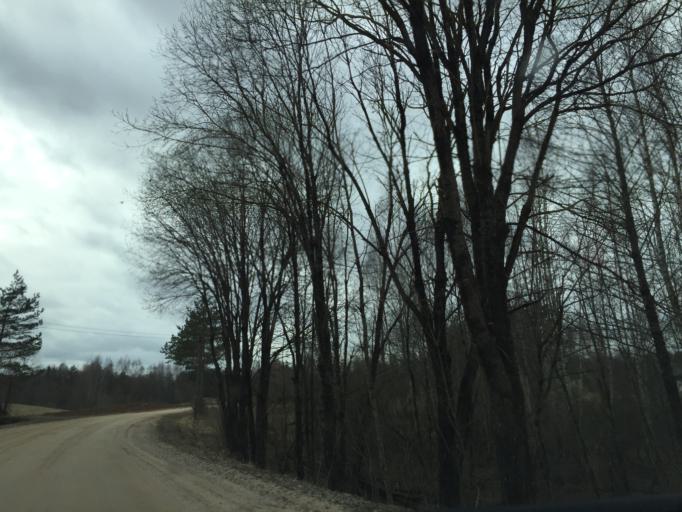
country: LV
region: Kraslavas Rajons
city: Kraslava
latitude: 55.9637
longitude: 27.0623
